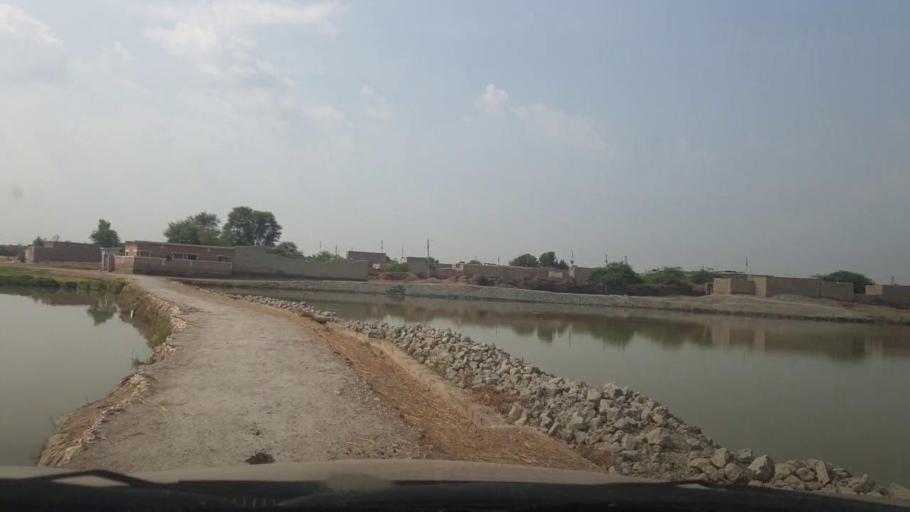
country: PK
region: Sindh
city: Larkana
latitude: 27.6501
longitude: 68.2102
